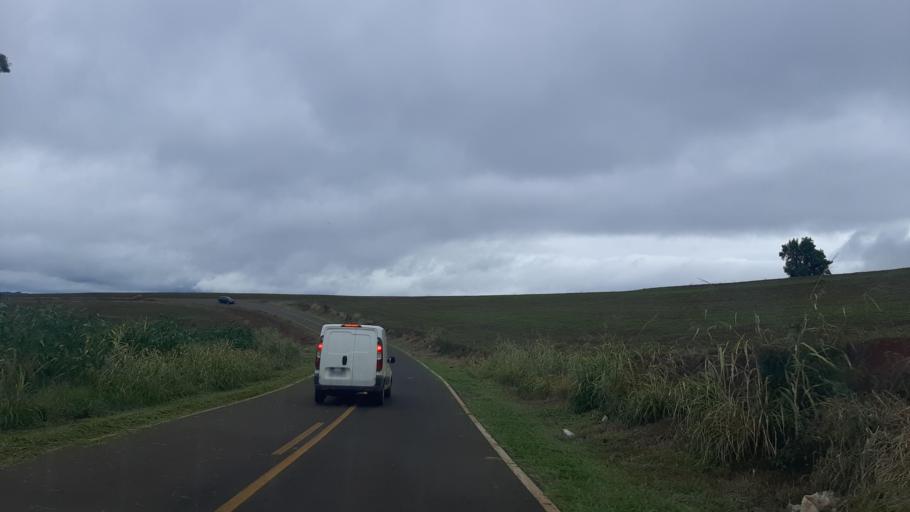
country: BR
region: Parana
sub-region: Ampere
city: Ampere
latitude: -25.9530
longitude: -53.4579
